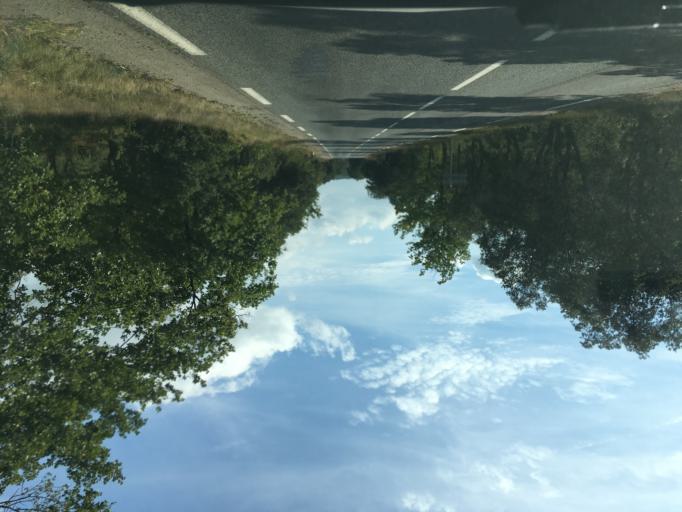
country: FR
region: Provence-Alpes-Cote d'Azur
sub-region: Departement du Var
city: Villecroze
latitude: 43.5449
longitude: 6.3237
